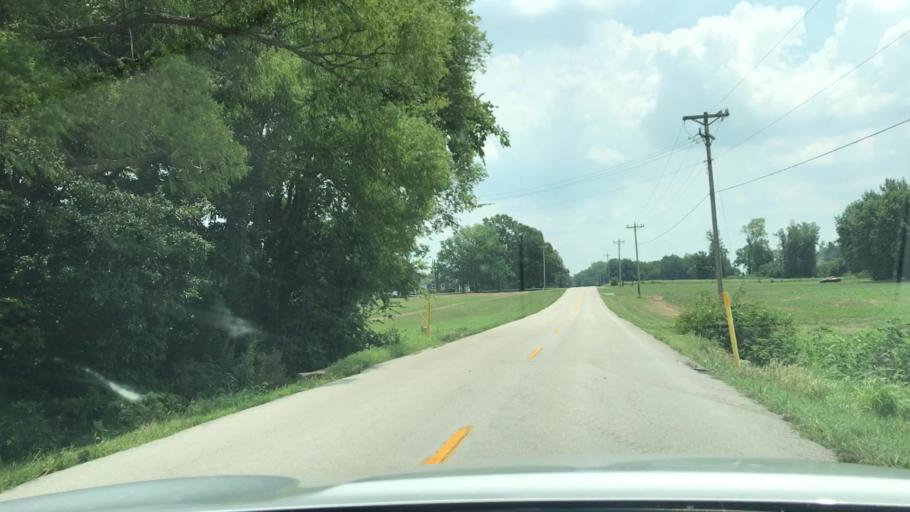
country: US
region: Kentucky
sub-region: Todd County
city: Elkton
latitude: 36.7650
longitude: -87.1088
